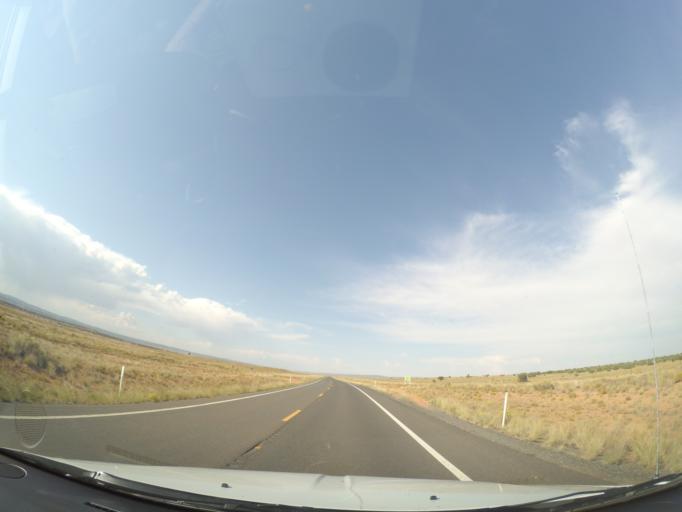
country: US
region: Arizona
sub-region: Coconino County
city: Tuba City
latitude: 36.3541
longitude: -111.4243
